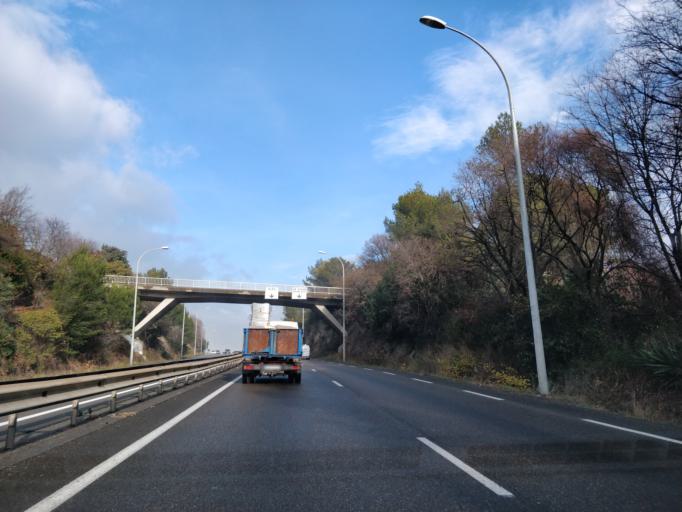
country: FR
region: Languedoc-Roussillon
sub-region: Departement du Gard
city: Nimes
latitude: 43.8347
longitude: 4.3218
